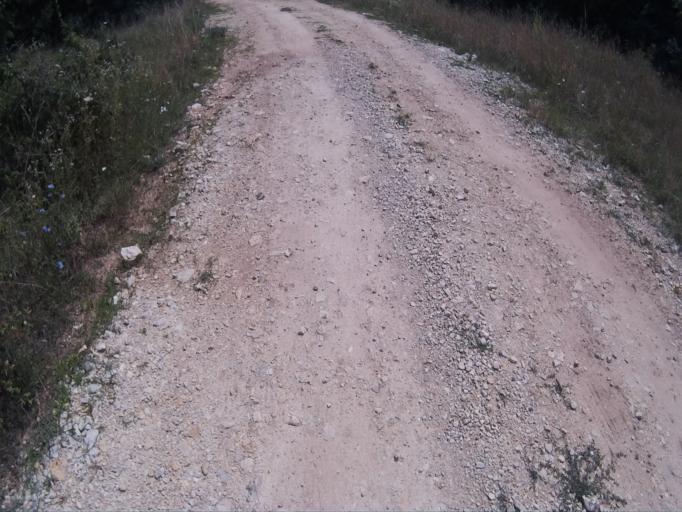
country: HU
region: Veszprem
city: Papa
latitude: 47.2915
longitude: 17.6296
